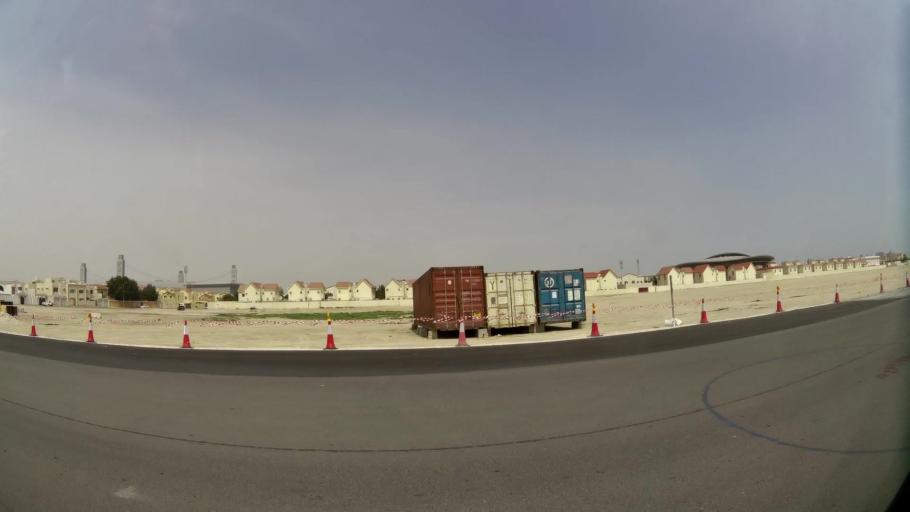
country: QA
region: Baladiyat ad Dawhah
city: Doha
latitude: 25.2649
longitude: 51.4886
